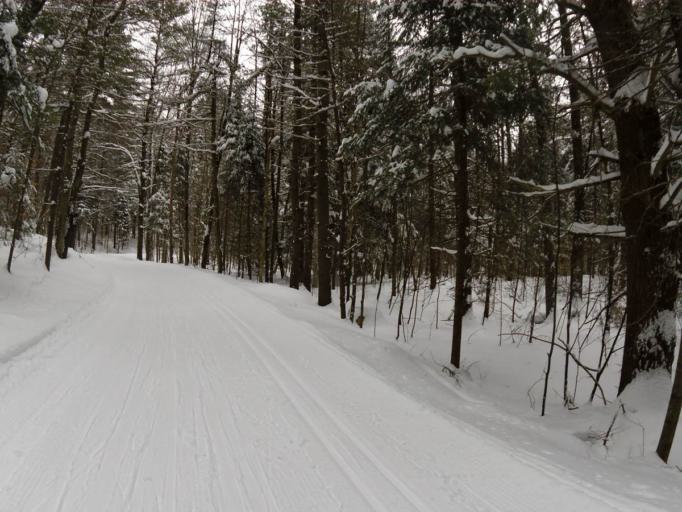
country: CA
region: Quebec
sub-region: Outaouais
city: Wakefield
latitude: 45.5975
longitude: -76.0165
